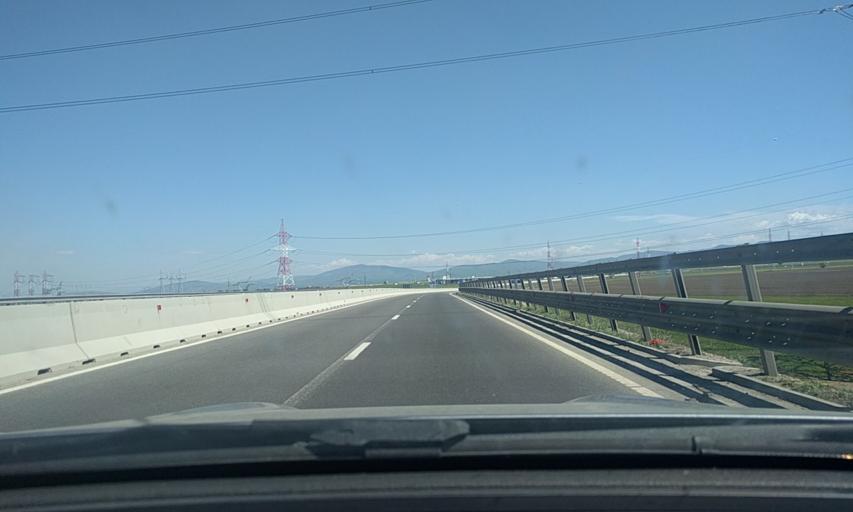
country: RO
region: Brasov
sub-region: Comuna Sanpetru
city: Sanpetru
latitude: 45.6885
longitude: 25.6488
